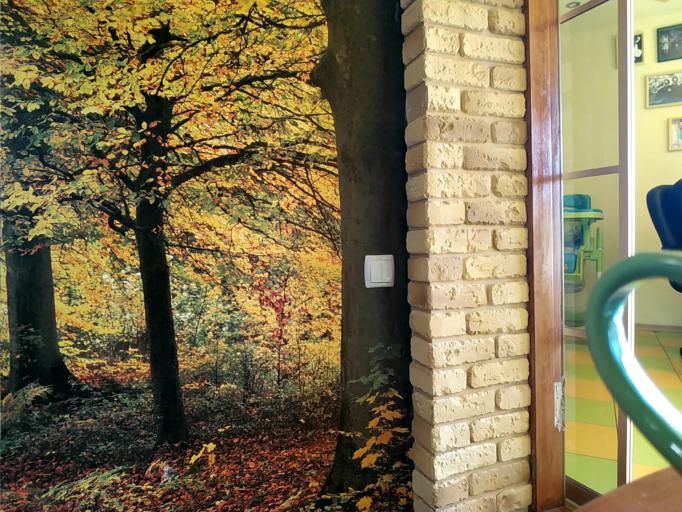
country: RU
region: Moskovskaya
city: Krasnoarmeysk
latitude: 56.0697
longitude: 38.1572
